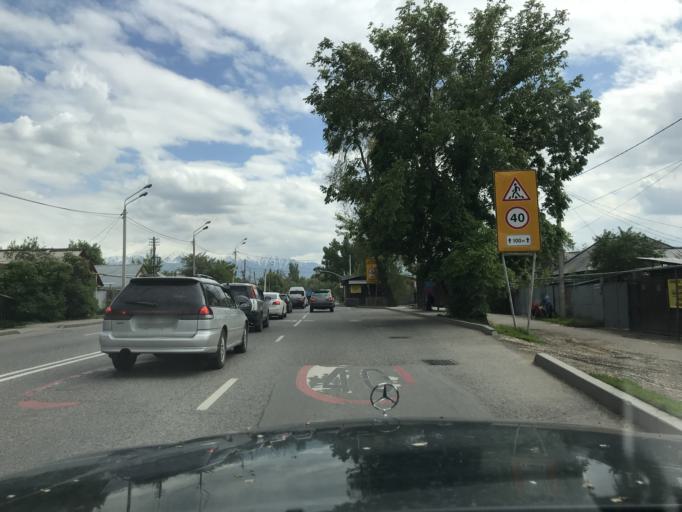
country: KZ
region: Almaty Qalasy
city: Almaty
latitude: 43.2932
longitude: 76.9002
